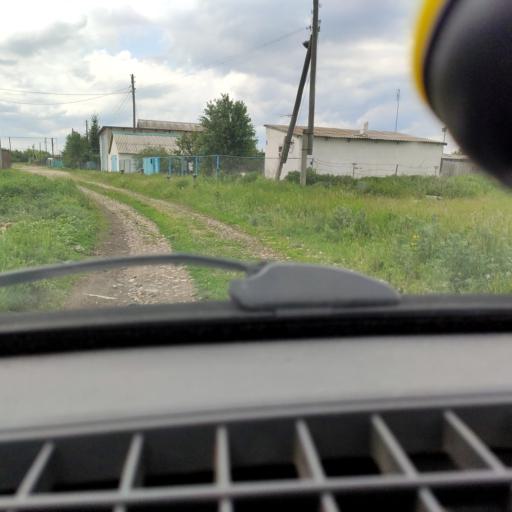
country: RU
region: Samara
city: Povolzhskiy
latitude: 53.6486
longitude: 49.6969
